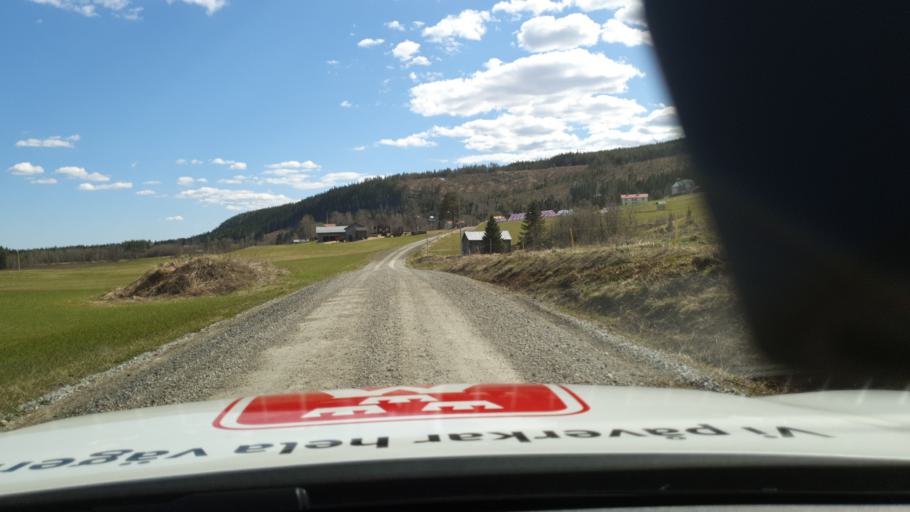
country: SE
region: Jaemtland
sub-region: Bergs Kommun
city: Hoverberg
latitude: 62.9434
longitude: 14.2703
